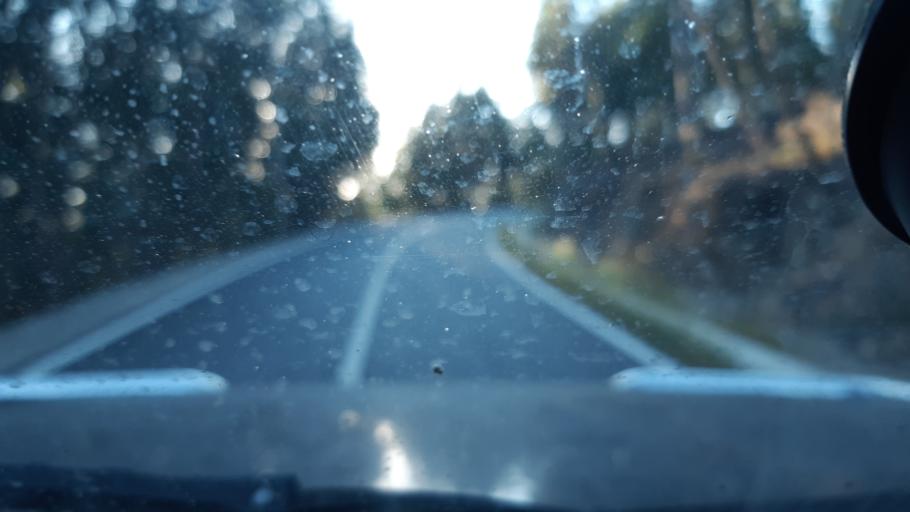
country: PT
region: Viseu
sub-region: Mortagua
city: Mortagua
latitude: 40.5336
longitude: -8.2461
